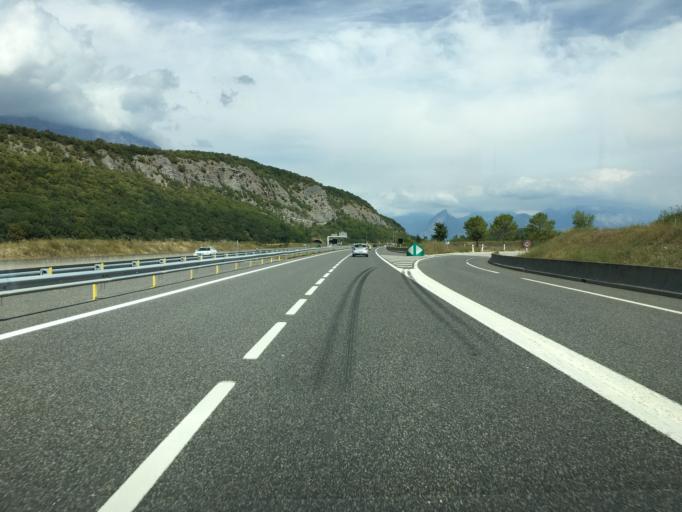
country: FR
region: Rhone-Alpes
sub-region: Departement de l'Isere
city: Vif
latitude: 45.0740
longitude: 5.6797
